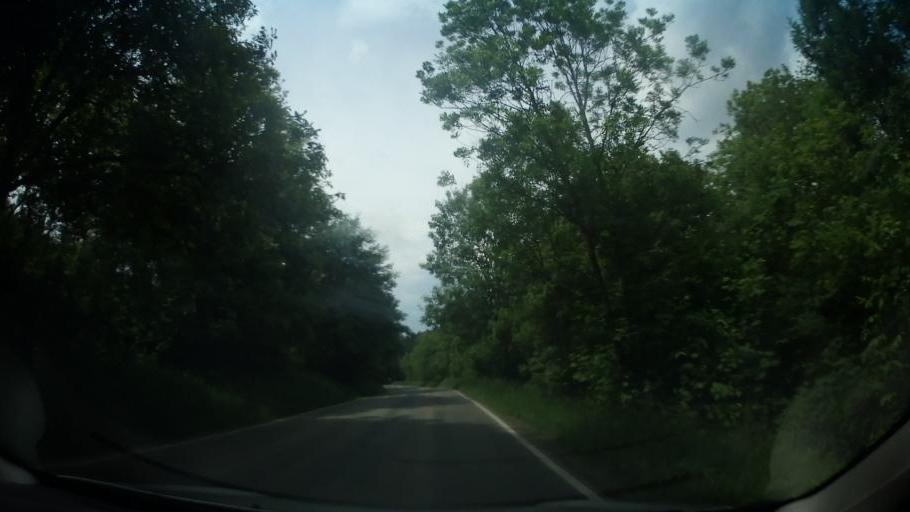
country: CZ
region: South Moravian
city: Lysice
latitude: 49.4517
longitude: 16.5227
